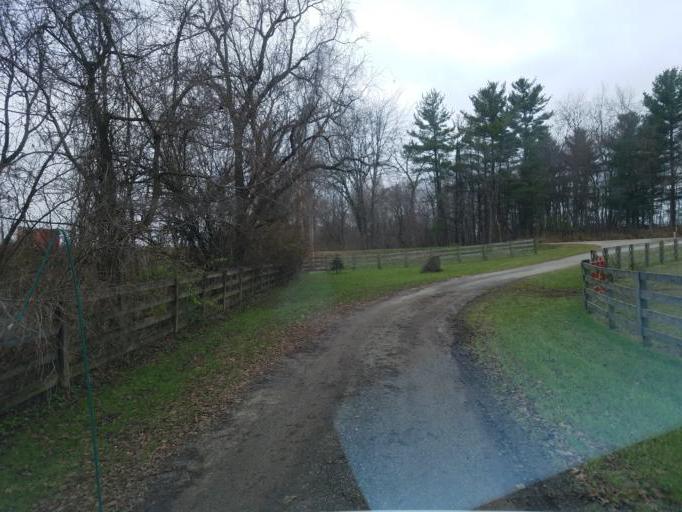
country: US
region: Ohio
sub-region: Morrow County
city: Cardington
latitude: 40.4264
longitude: -82.8536
